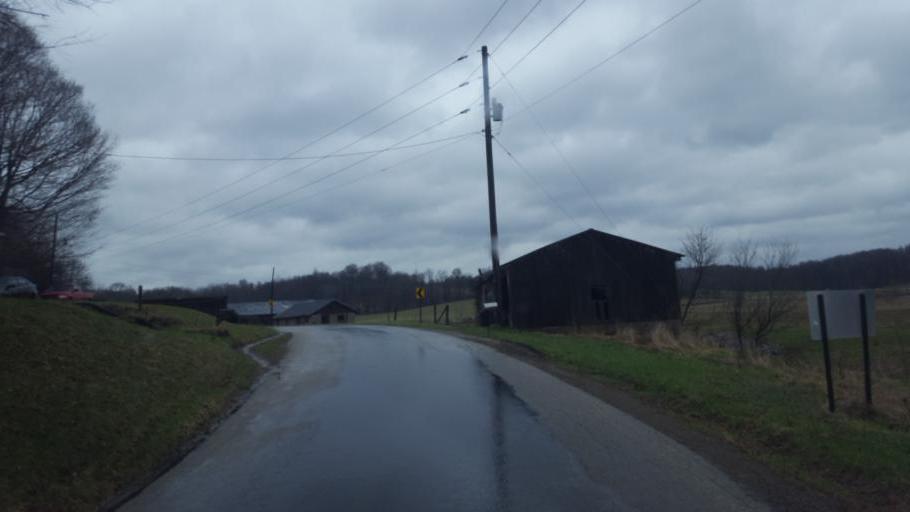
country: US
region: Ohio
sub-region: Sandusky County
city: Bellville
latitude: 40.5577
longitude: -82.4812
